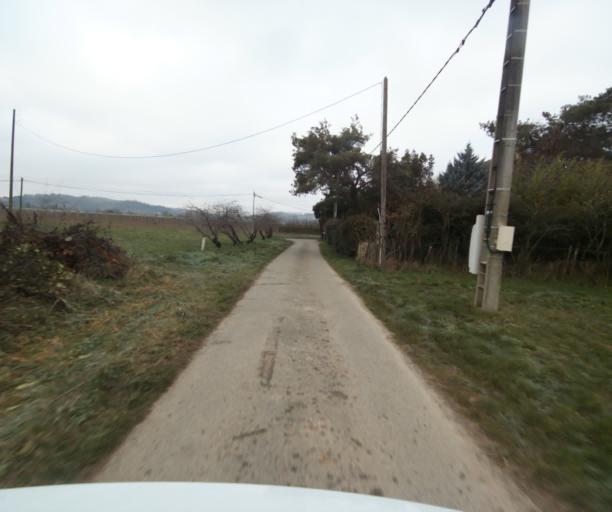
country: FR
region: Midi-Pyrenees
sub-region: Departement du Tarn-et-Garonne
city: Moissac
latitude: 44.1075
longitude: 1.1338
